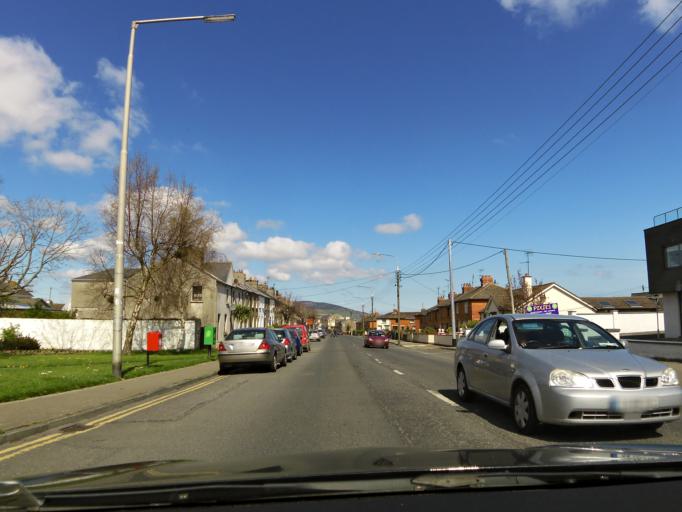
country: IE
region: Leinster
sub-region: Wicklow
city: Arklow
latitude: 52.7916
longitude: -6.1645
